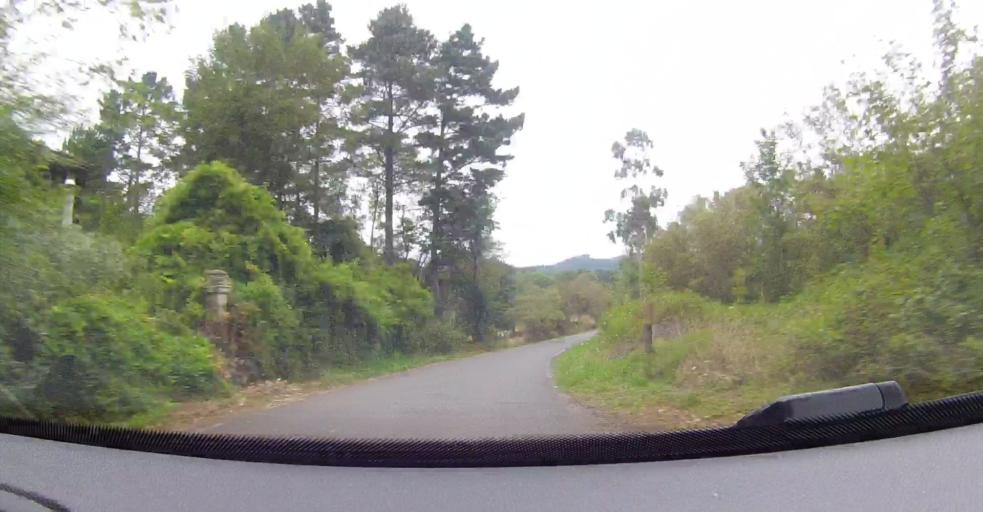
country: ES
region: Basque Country
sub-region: Bizkaia
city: Urrestieta
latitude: 43.2301
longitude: -3.1887
